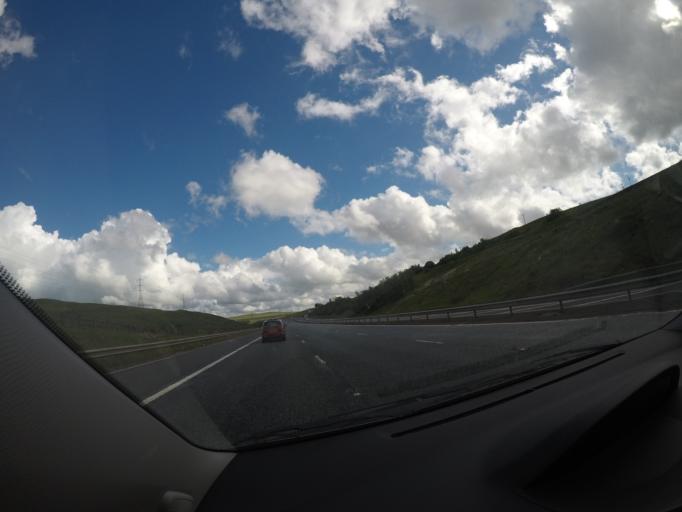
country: GB
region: Scotland
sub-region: South Lanarkshire
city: Douglas
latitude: 55.5553
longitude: -3.8016
